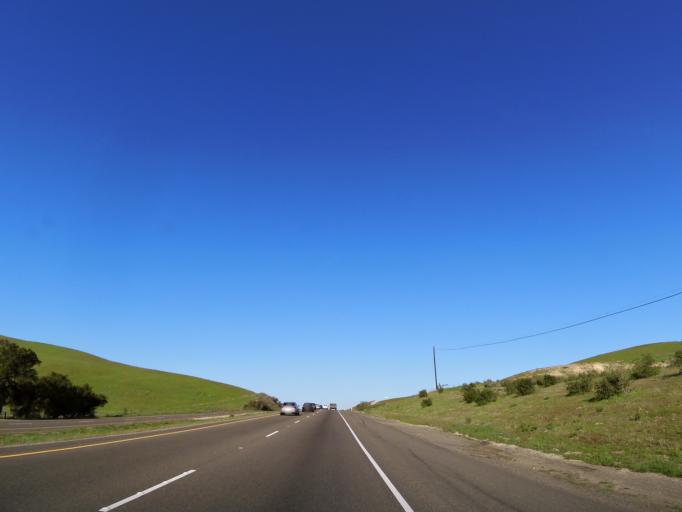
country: US
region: California
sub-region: Santa Barbara County
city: Orcutt
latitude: 34.8191
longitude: -120.3514
